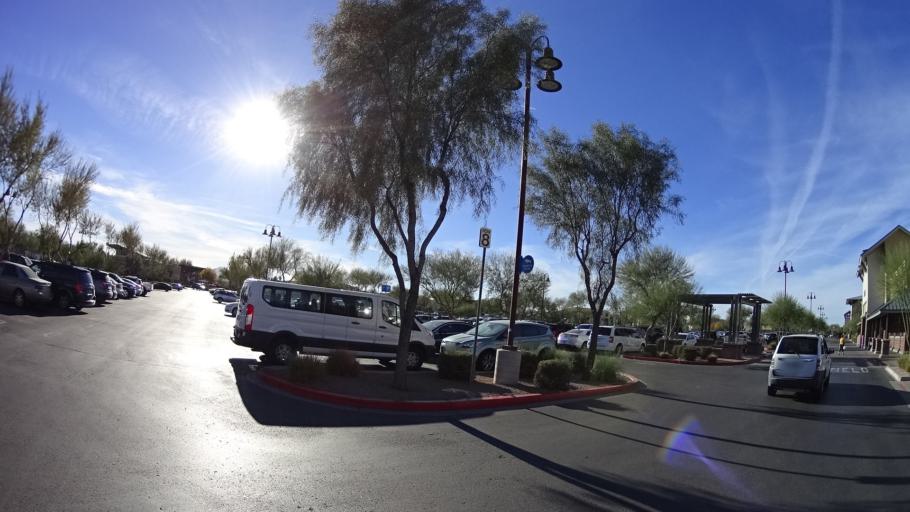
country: US
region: Arizona
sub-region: Maricopa County
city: Queen Creek
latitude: 33.2504
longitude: -111.6290
